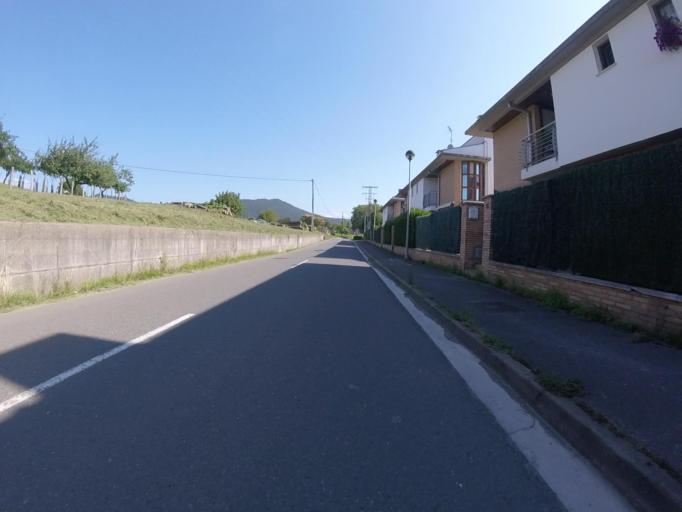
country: ES
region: Basque Country
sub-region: Provincia de Guipuzcoa
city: Astigarraga
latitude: 43.2792
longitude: -1.9131
